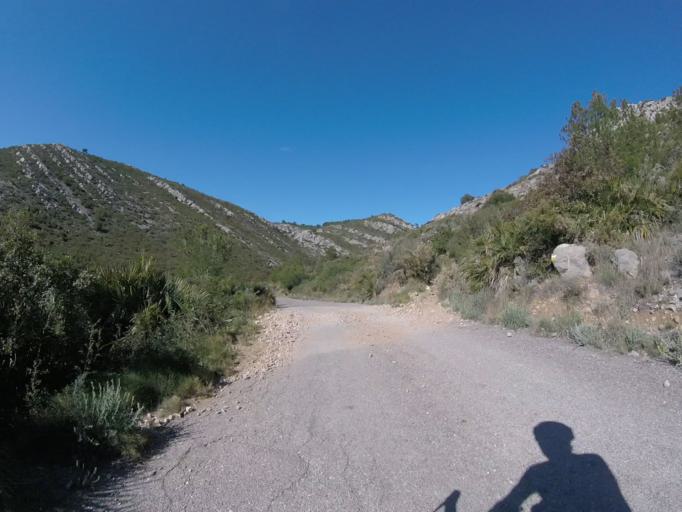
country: ES
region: Valencia
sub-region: Provincia de Castello
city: Orpesa/Oropesa del Mar
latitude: 40.0770
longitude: 0.1071
